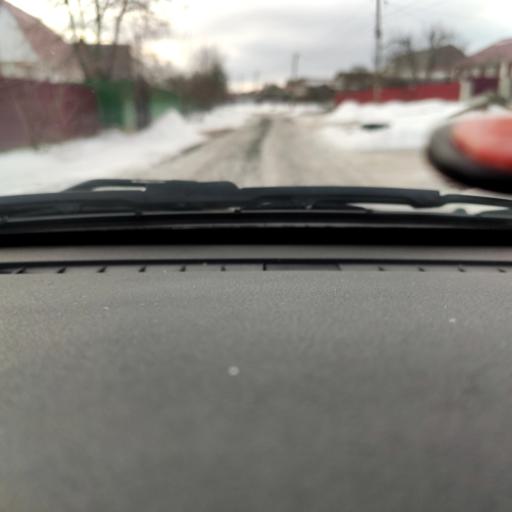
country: RU
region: Voronezj
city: Semiluki
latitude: 51.7155
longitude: 39.0346
